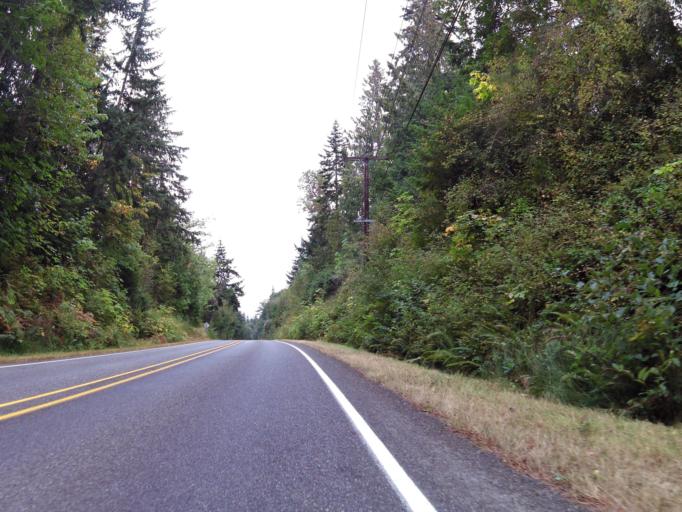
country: US
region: Washington
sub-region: Jefferson County
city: Port Hadlock-Irondale
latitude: 48.0088
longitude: -122.7288
